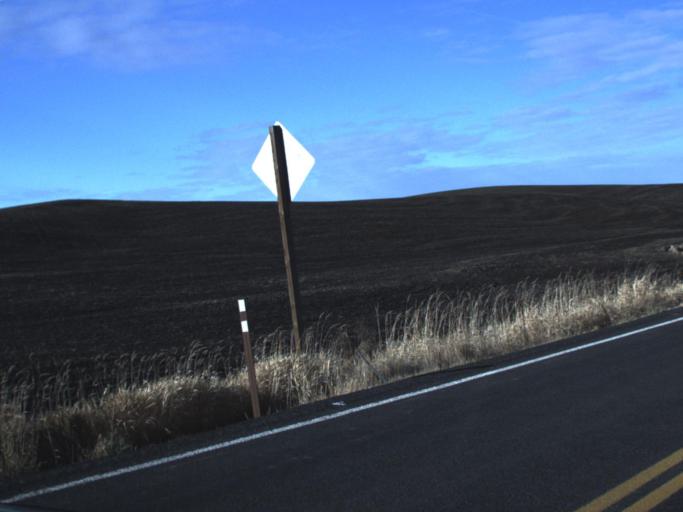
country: US
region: Washington
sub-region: Whitman County
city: Pullman
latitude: 46.7087
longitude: -117.2703
